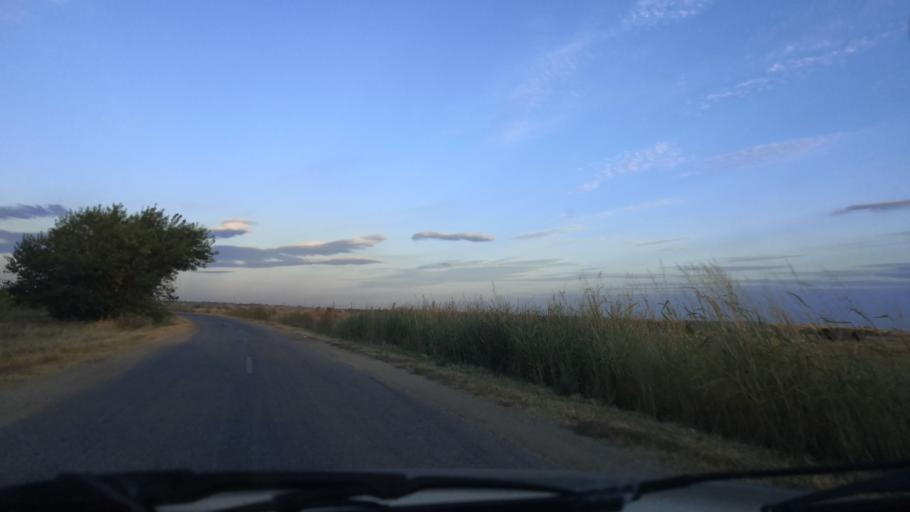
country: RO
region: Mehedinti
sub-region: Comuna Gruia
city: Izvoarele
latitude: 44.2642
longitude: 22.6507
